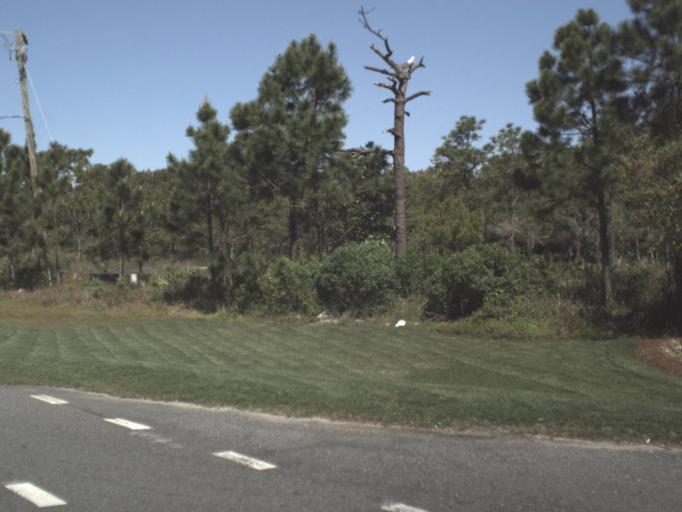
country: US
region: Florida
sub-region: Walton County
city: Miramar Beach
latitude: 30.3880
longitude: -86.4104
